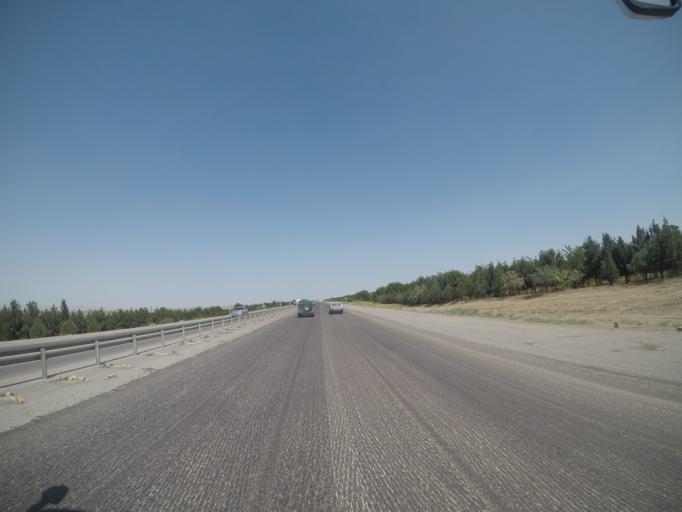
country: AZ
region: Haciqabul
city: Haciqabul
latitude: 40.0459
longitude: 49.0052
